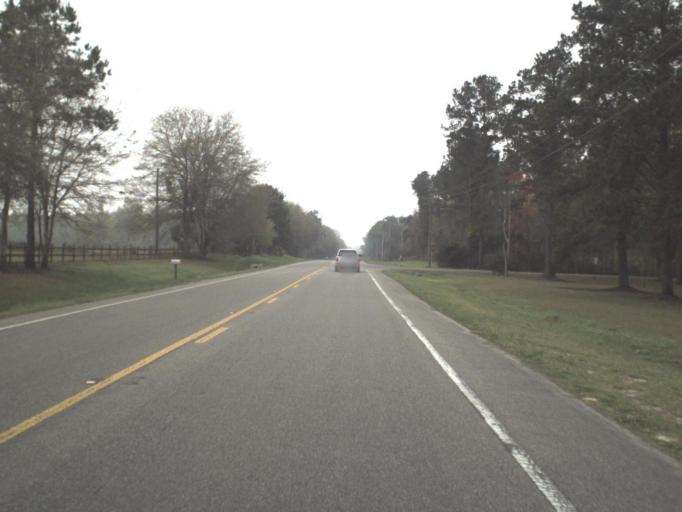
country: US
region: Florida
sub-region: Gadsden County
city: Gretna
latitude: 30.5601
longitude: -84.6772
